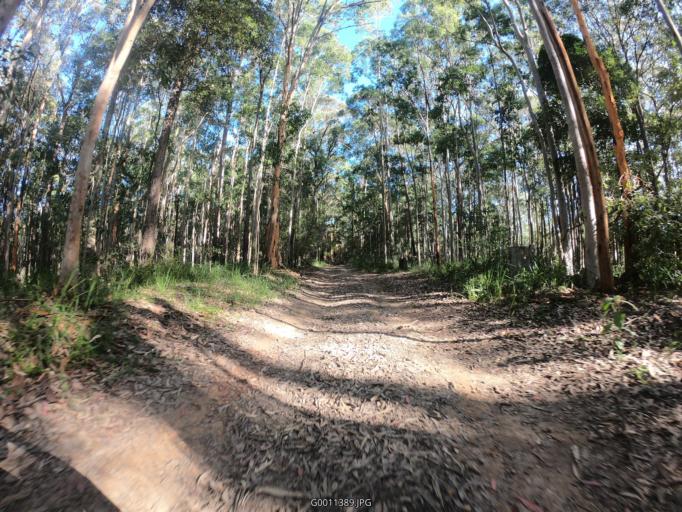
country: AU
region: New South Wales
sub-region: Lake Macquarie Shire
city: Cooranbong
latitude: -33.0266
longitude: 151.3027
